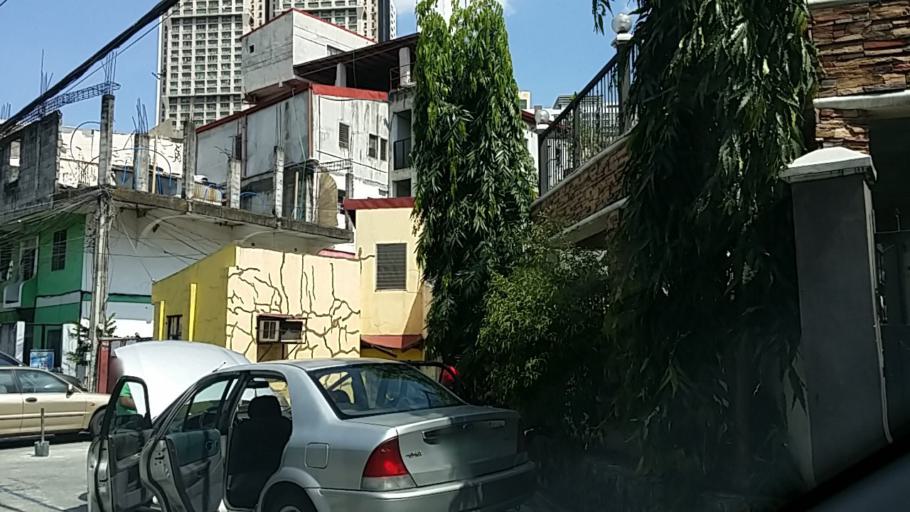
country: PH
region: Metro Manila
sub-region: Mandaluyong
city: Mandaluyong City
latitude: 14.5750
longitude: 121.0457
